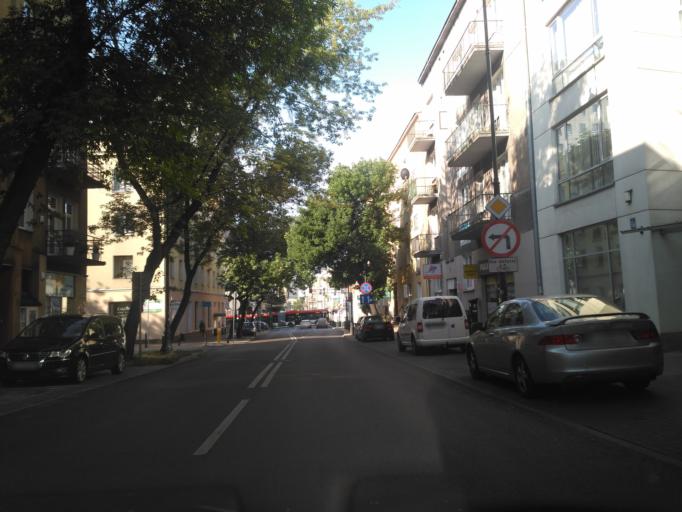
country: PL
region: Lublin Voivodeship
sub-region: Powiat lubelski
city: Lublin
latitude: 51.2427
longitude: 22.5560
